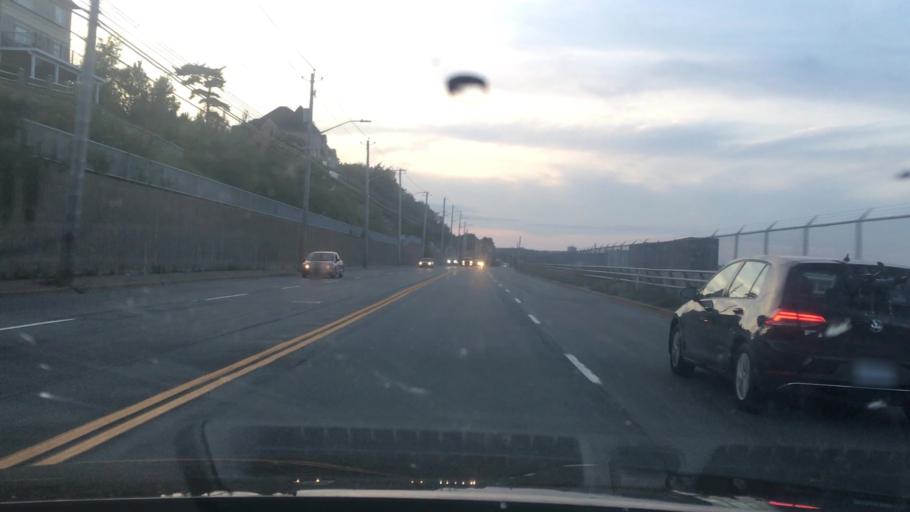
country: CA
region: Nova Scotia
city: Dartmouth
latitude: 44.6673
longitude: -63.6379
